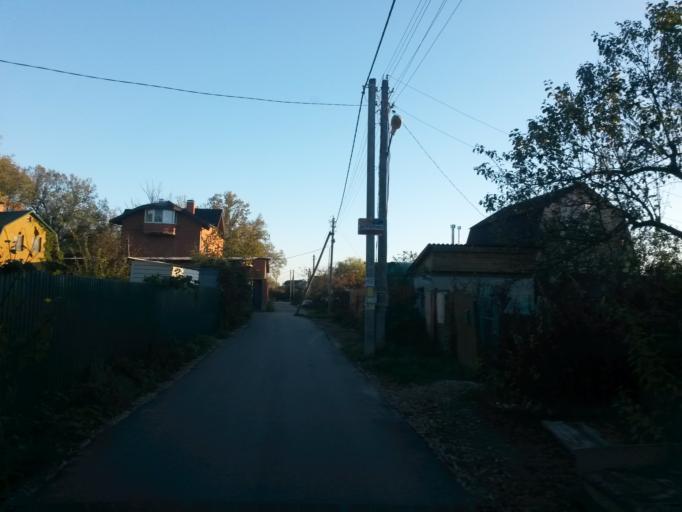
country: RU
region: Moskovskaya
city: Lyubuchany
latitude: 55.2428
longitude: 37.6370
